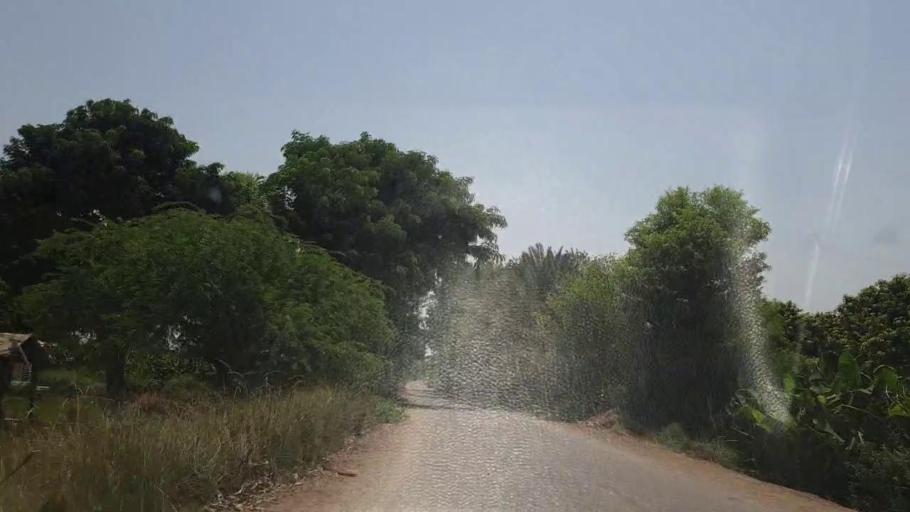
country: PK
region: Sindh
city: Kot Diji
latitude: 27.2795
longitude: 68.6483
